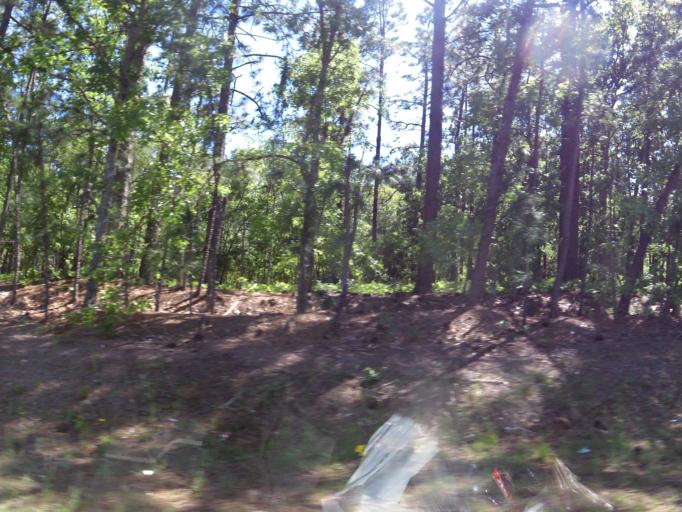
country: US
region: South Carolina
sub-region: Aiken County
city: New Ellenton
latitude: 33.5065
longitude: -81.5476
